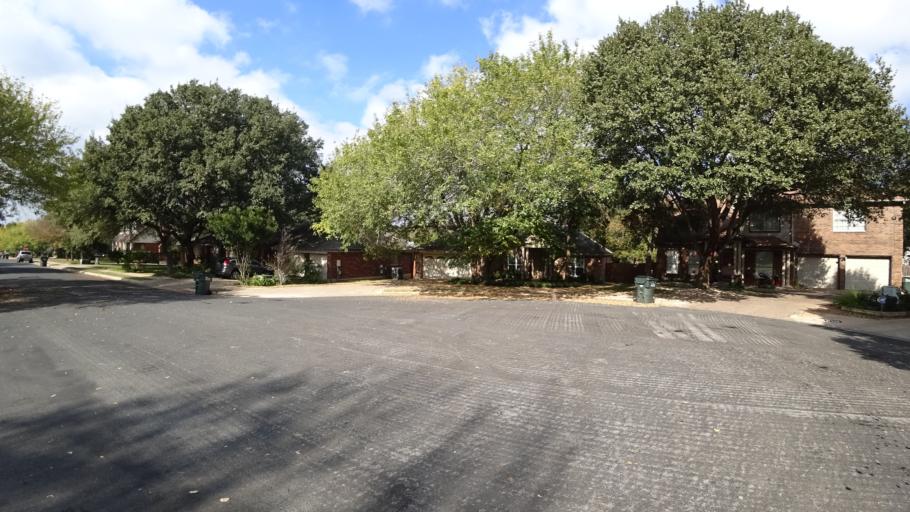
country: US
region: Texas
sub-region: Travis County
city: Shady Hollow
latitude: 30.1593
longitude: -97.8506
